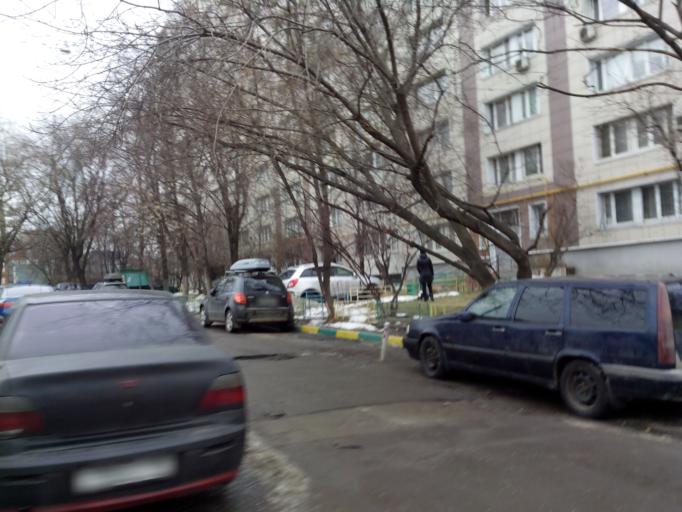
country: RU
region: Moscow
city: Lefortovo
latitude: 55.7770
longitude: 37.6911
